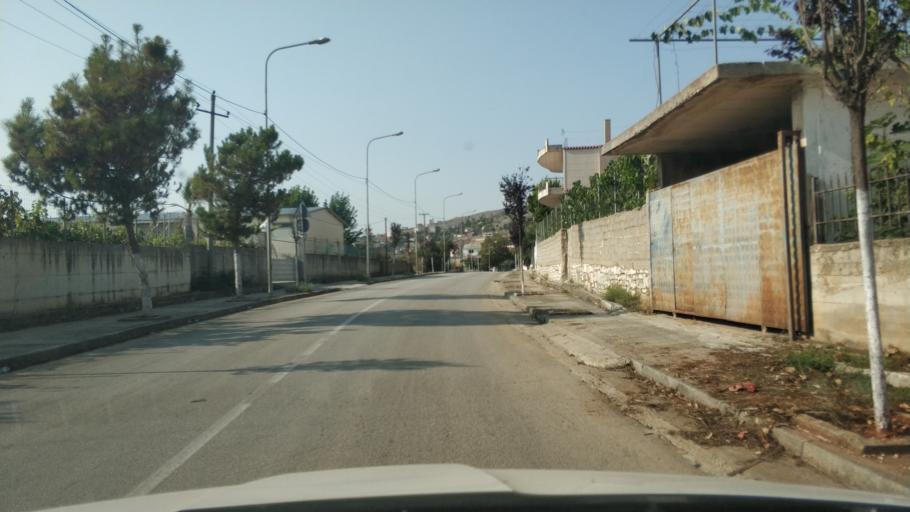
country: AL
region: Vlore
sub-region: Rrethi i Sarandes
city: Sarande
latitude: 39.8428
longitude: 20.0349
